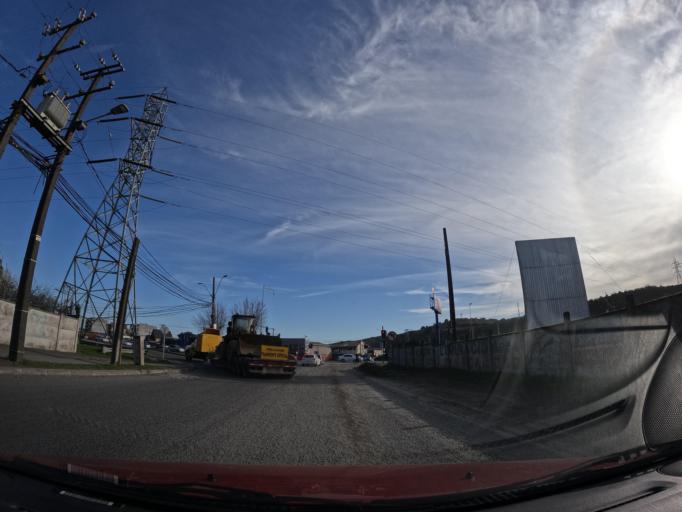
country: CL
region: Biobio
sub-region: Provincia de Concepcion
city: Talcahuano
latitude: -36.7682
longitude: -73.0837
